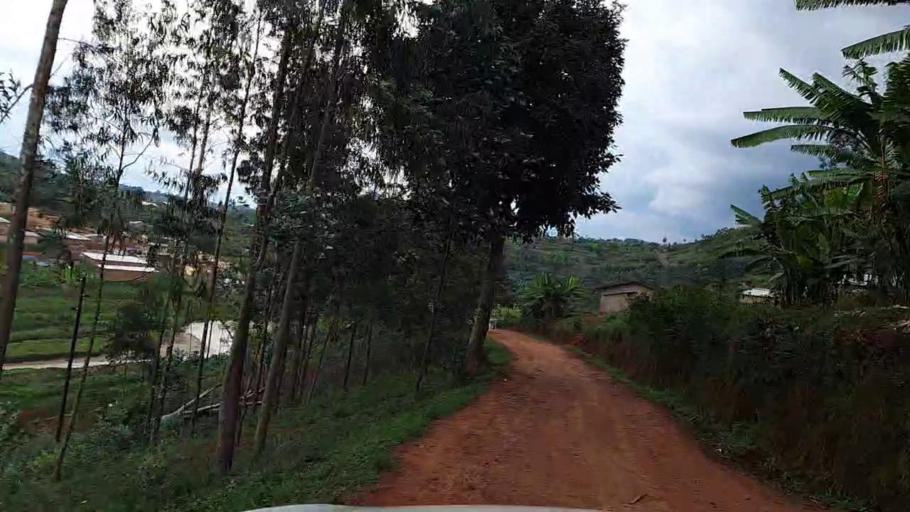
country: RW
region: Southern Province
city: Gikongoro
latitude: -2.4170
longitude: 29.6618
